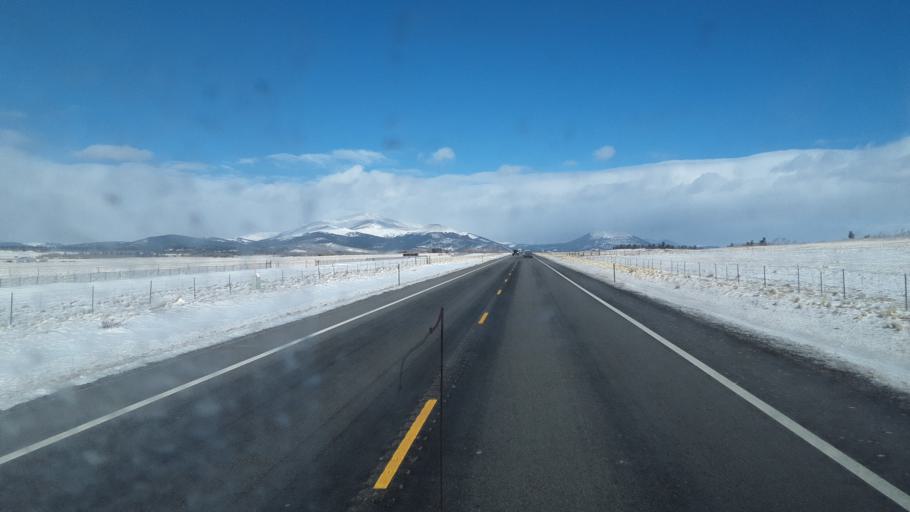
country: US
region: Colorado
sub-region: Park County
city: Fairplay
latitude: 39.1901
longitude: -105.9977
